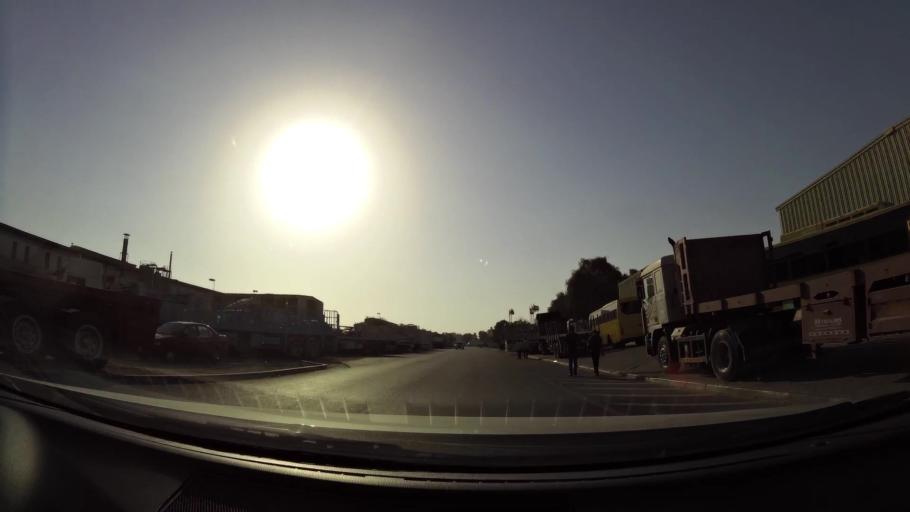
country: AE
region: Dubai
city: Dubai
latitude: 25.1313
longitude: 55.2438
